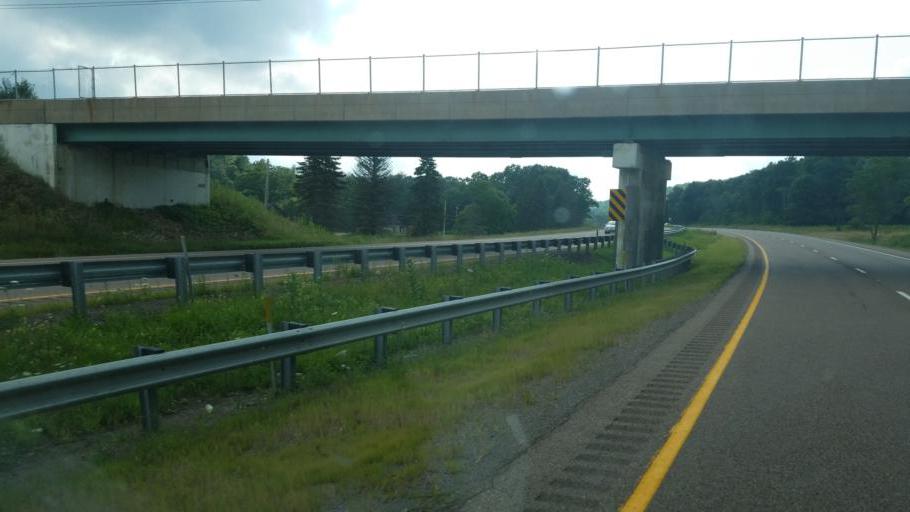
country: US
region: Pennsylvania
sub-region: Somerset County
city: Meyersdale
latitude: 39.7017
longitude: -79.3062
